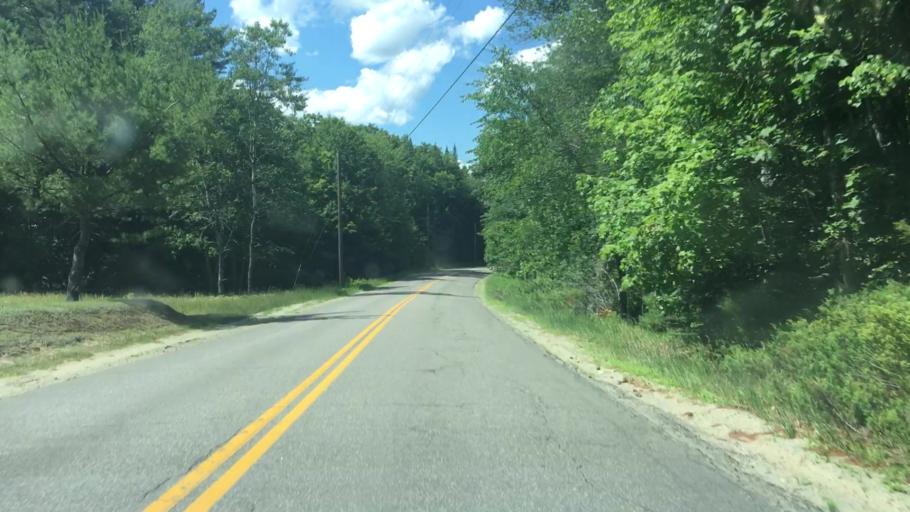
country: US
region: Maine
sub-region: Franklin County
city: Chesterville
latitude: 44.5711
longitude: -70.0886
